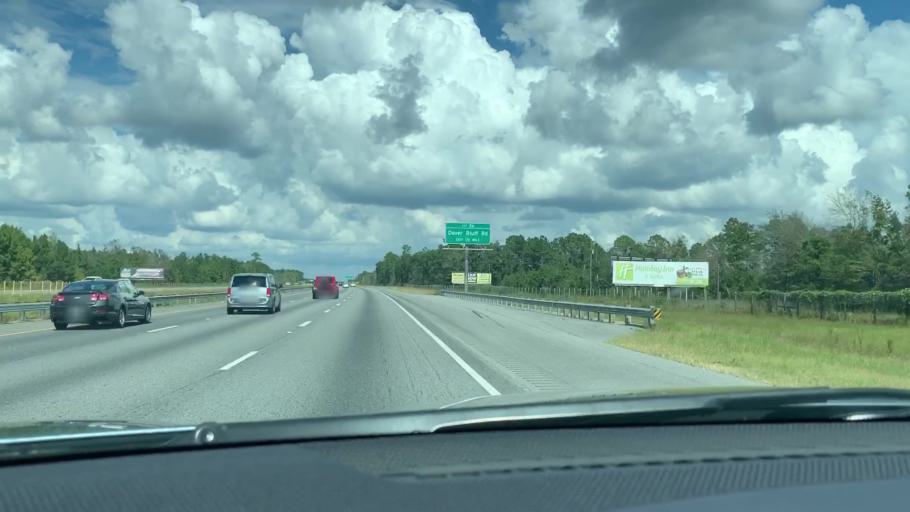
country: US
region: Georgia
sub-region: Glynn County
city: Brunswick
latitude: 31.0915
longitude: -81.6044
